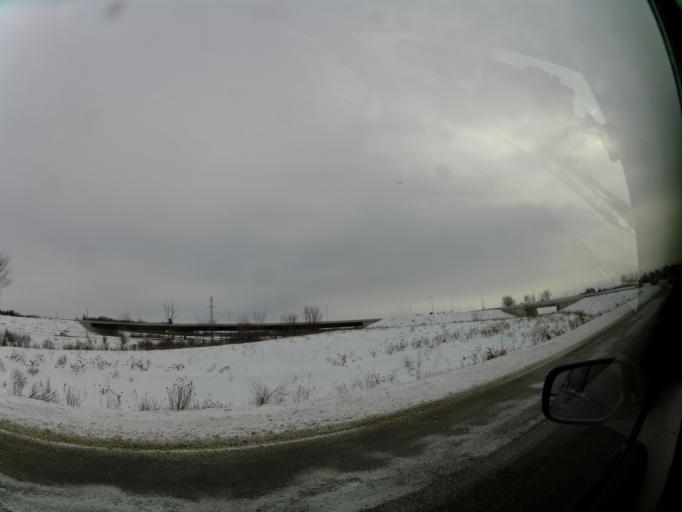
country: CA
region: Ontario
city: Ottawa
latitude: 45.3846
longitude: -75.5878
